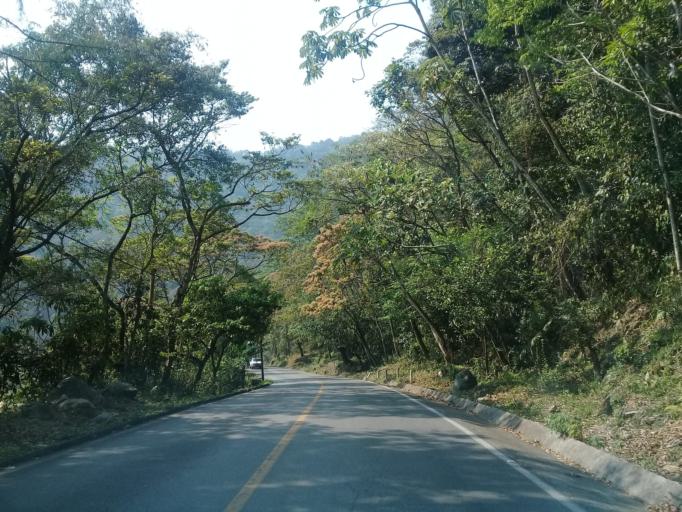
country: MX
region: Veracruz
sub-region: Ixtaczoquitlan
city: Campo Chico
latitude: 18.8435
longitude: -97.0279
